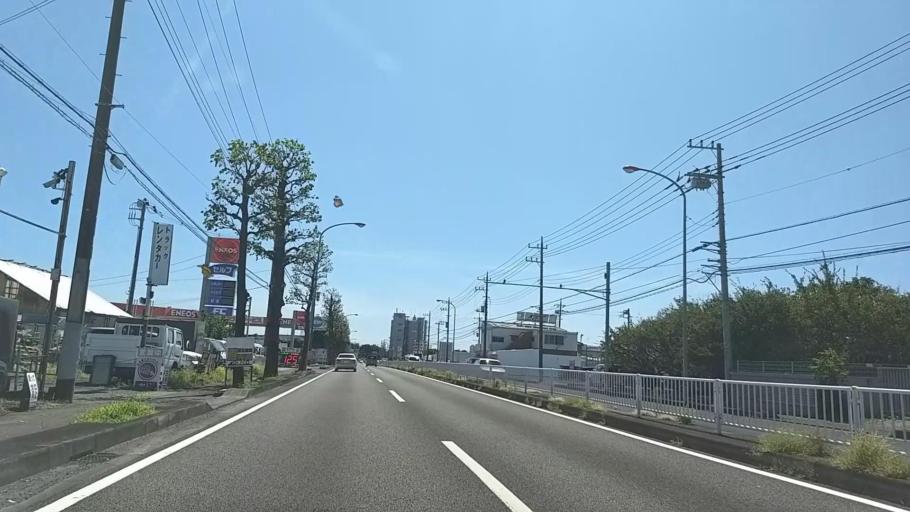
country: JP
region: Kanagawa
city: Zama
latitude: 35.5457
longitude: 139.3580
